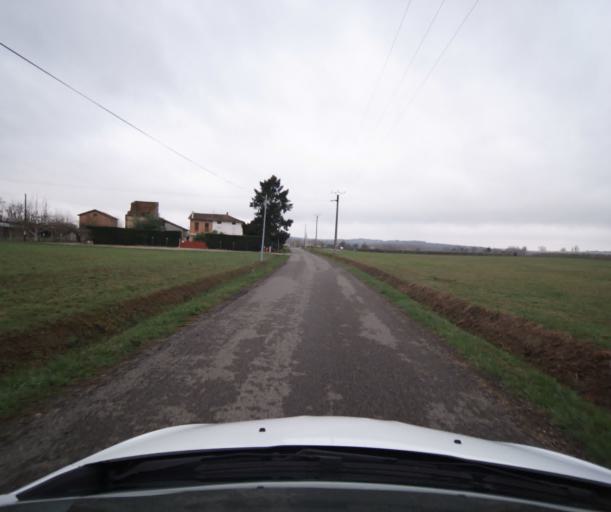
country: FR
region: Midi-Pyrenees
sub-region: Departement du Tarn-et-Garonne
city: Moissac
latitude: 44.0827
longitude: 1.1199
